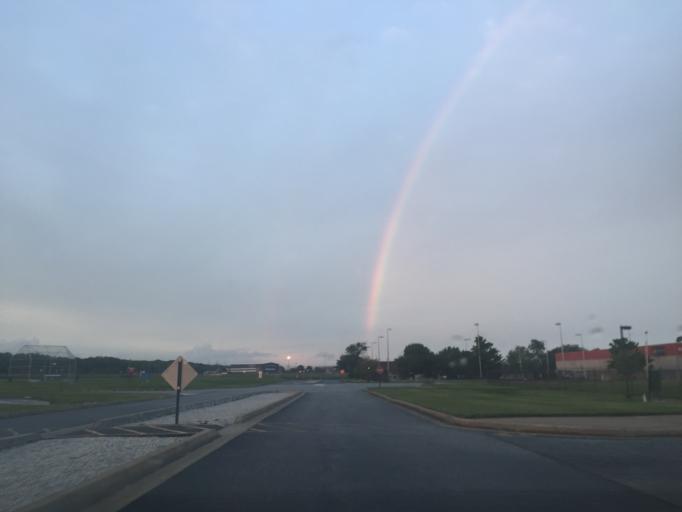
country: US
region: Maryland
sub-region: Baltimore County
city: Middle River
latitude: 39.3326
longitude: -76.4310
